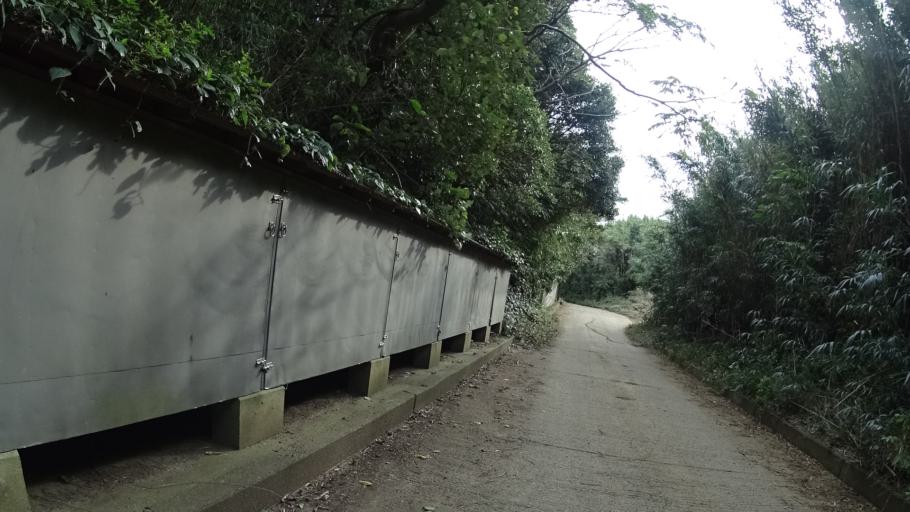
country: JP
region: Kanagawa
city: Miura
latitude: 35.1422
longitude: 139.6607
